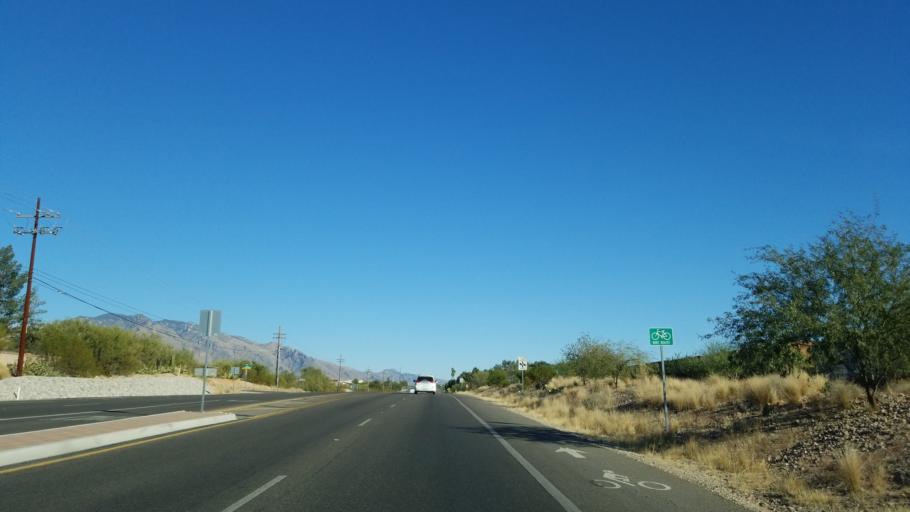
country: US
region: Arizona
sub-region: Pima County
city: Casas Adobes
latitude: 32.3231
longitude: -111.0205
